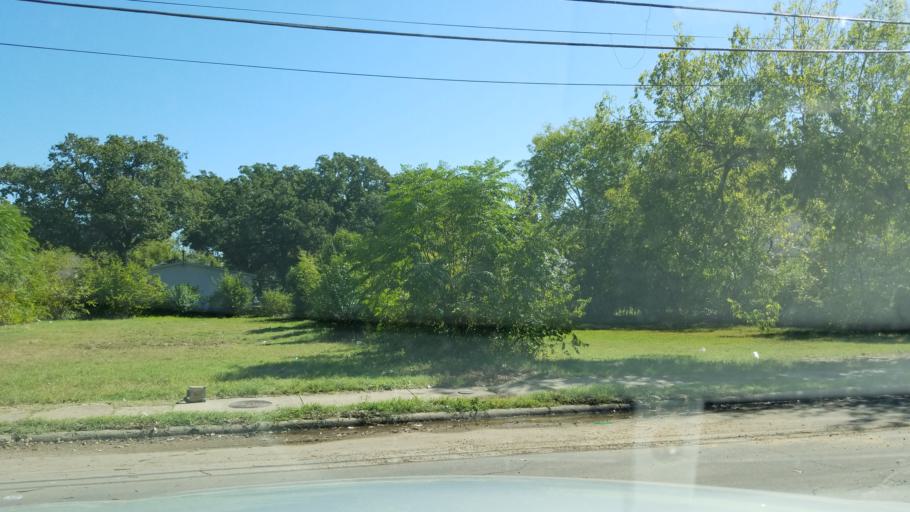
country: US
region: Texas
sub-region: Dallas County
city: Dallas
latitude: 32.7768
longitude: -96.7491
